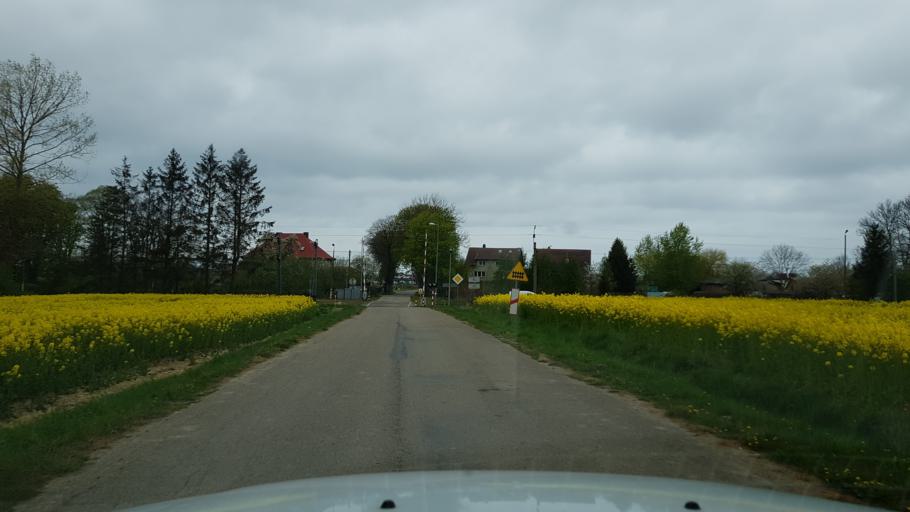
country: PL
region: West Pomeranian Voivodeship
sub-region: Powiat kolobrzeski
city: Ustronie Morskie
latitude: 54.1999
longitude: 15.7515
